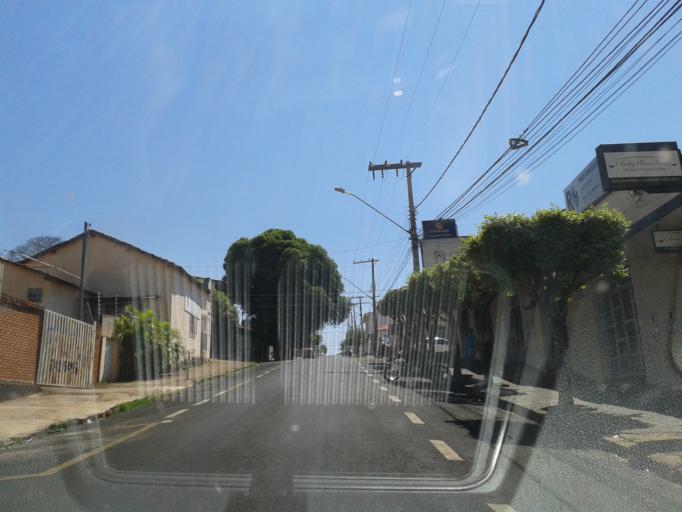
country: BR
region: Minas Gerais
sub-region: Araguari
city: Araguari
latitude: -18.6456
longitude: -48.1903
